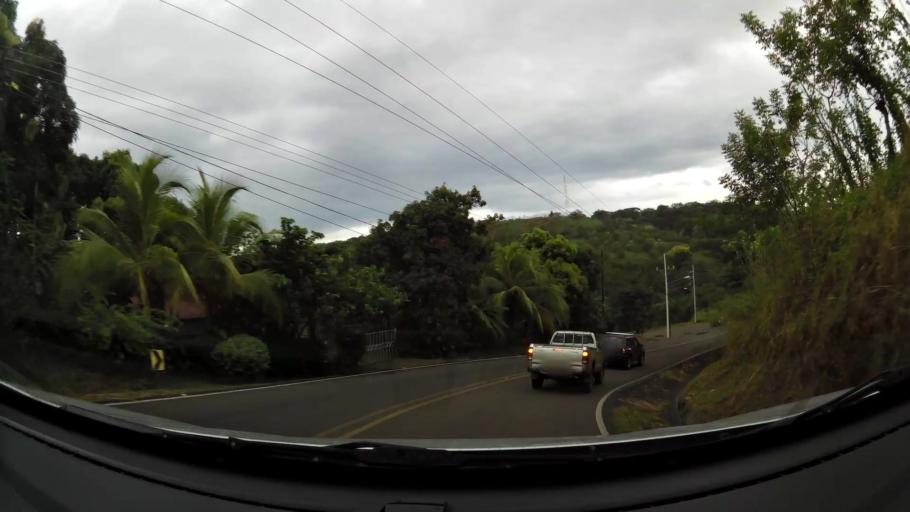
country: CR
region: Alajuela
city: Orotina
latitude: 9.9552
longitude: -84.5696
